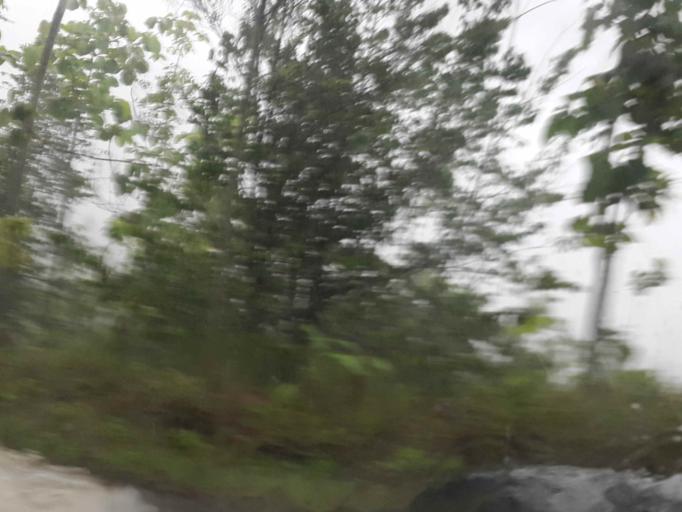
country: ID
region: Central Java
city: Kutoarjo
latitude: -7.5754
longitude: 109.7431
